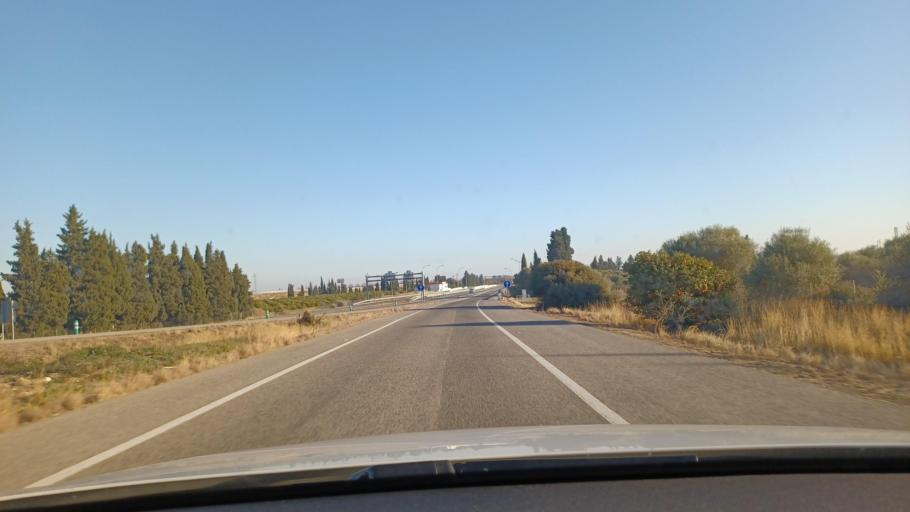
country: ES
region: Catalonia
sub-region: Provincia de Tarragona
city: Amposta
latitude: 40.7297
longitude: 0.5852
